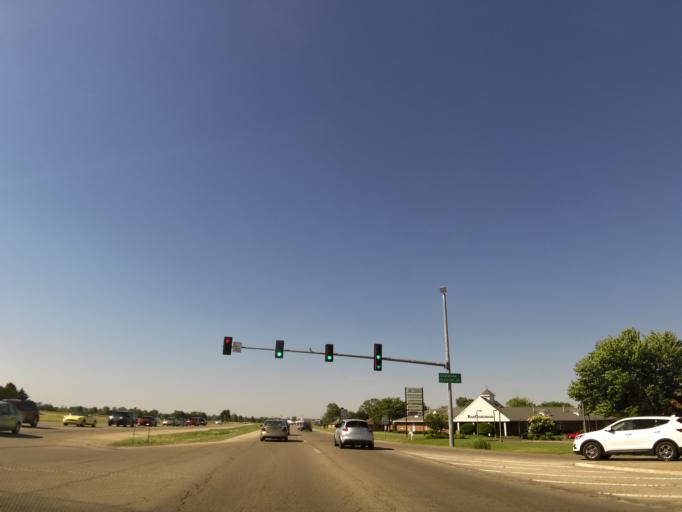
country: US
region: Illinois
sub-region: Winnebago County
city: Roscoe
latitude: 42.4291
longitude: -89.0164
